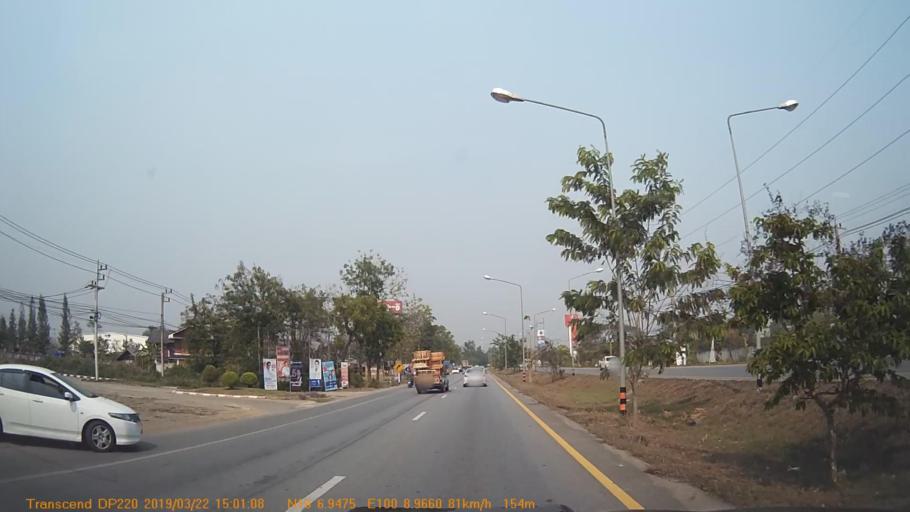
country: TH
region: Phrae
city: Phrae
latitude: 18.1160
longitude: 100.1498
